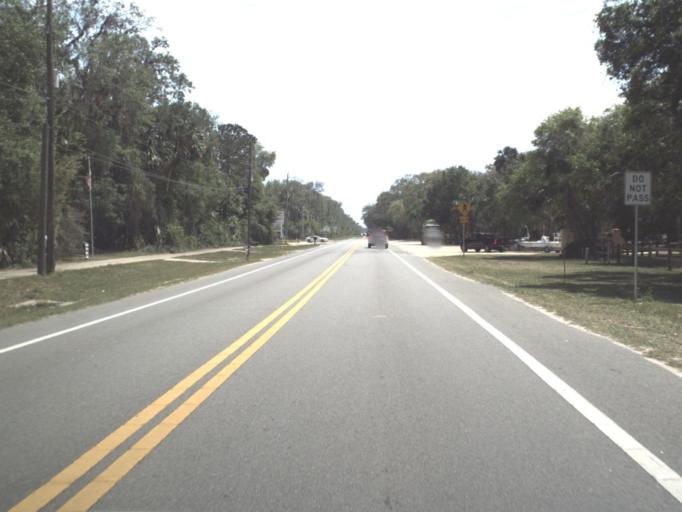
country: US
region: Florida
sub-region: Flagler County
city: Palm Coast
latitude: 29.6170
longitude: -81.2035
